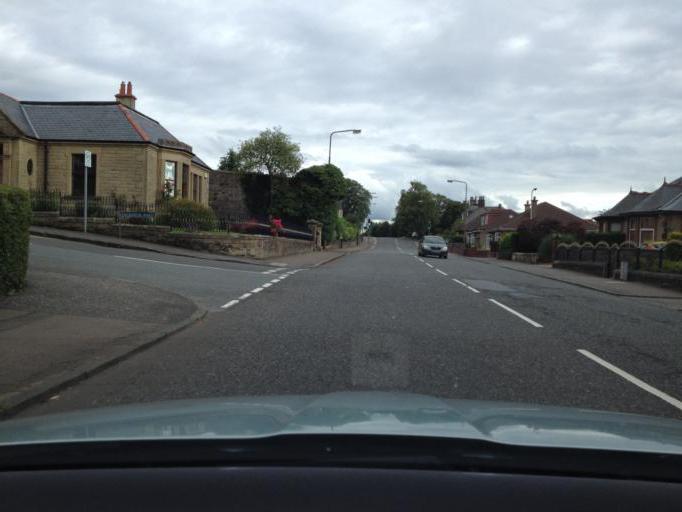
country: GB
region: Scotland
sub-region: West Lothian
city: Bathgate
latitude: 55.9010
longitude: -3.6355
